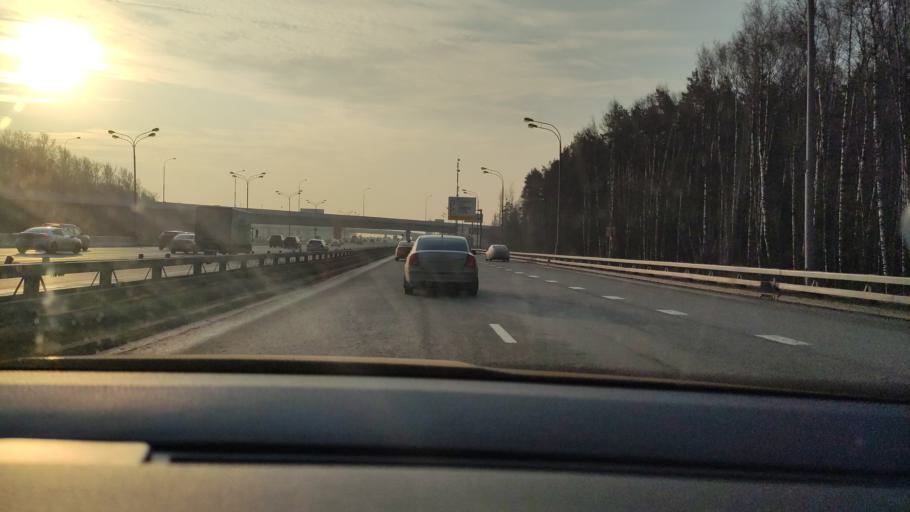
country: RU
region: Moskovskaya
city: Vostryakovo
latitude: 55.6425
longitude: 37.4539
